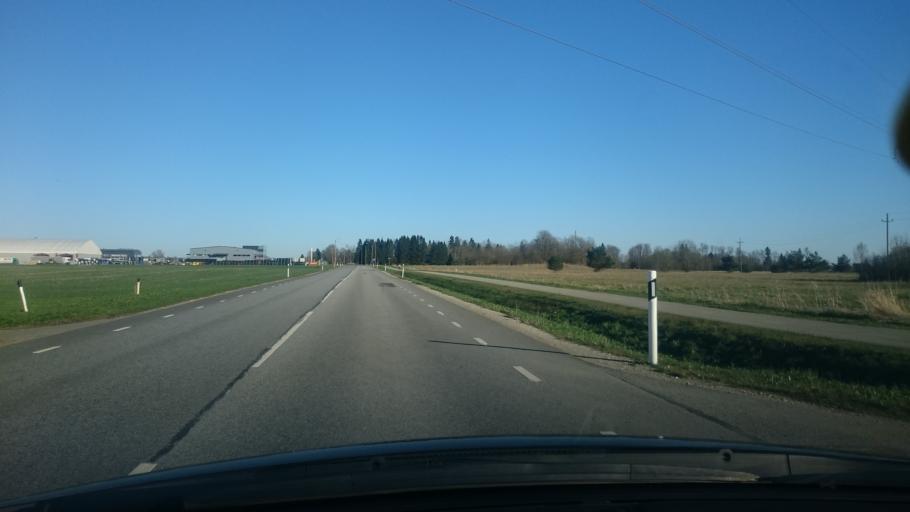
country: EE
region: Harju
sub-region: Kiili vald
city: Kiili
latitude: 59.3404
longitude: 24.8094
